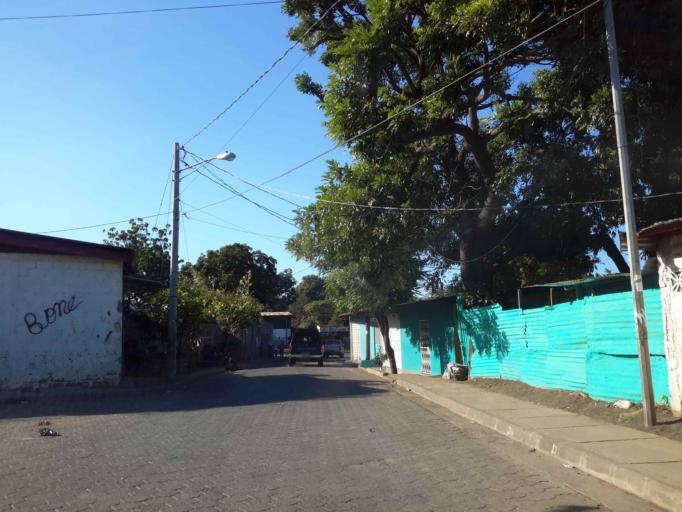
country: NI
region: Managua
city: Managua
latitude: 12.1331
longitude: -86.2891
